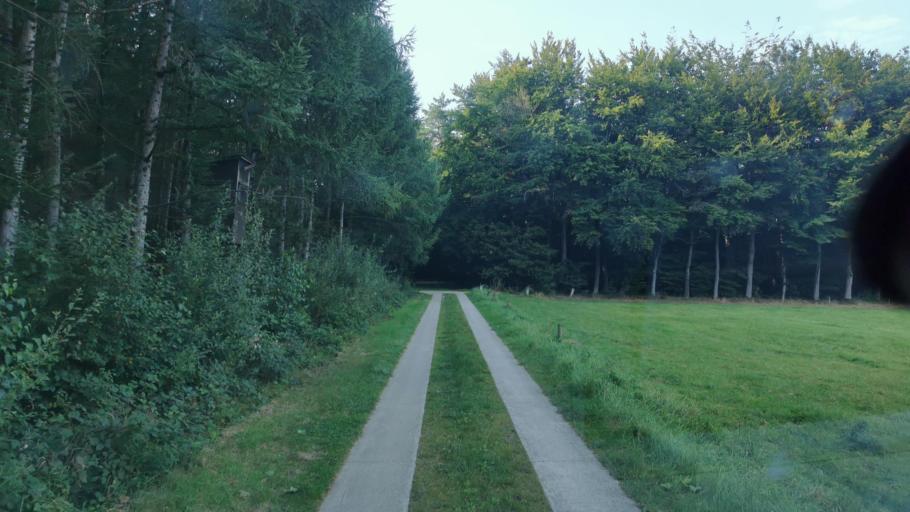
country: NL
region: Overijssel
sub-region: Gemeente Losser
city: Losser
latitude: 52.2910
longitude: 6.9726
